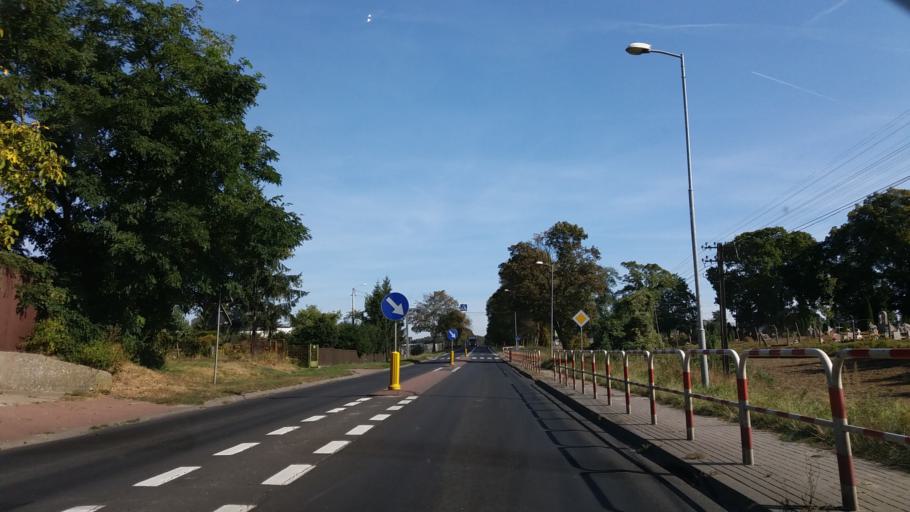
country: PL
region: Greater Poland Voivodeship
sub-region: Powiat miedzychodzki
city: Miedzychod
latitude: 52.5644
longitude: 15.9612
